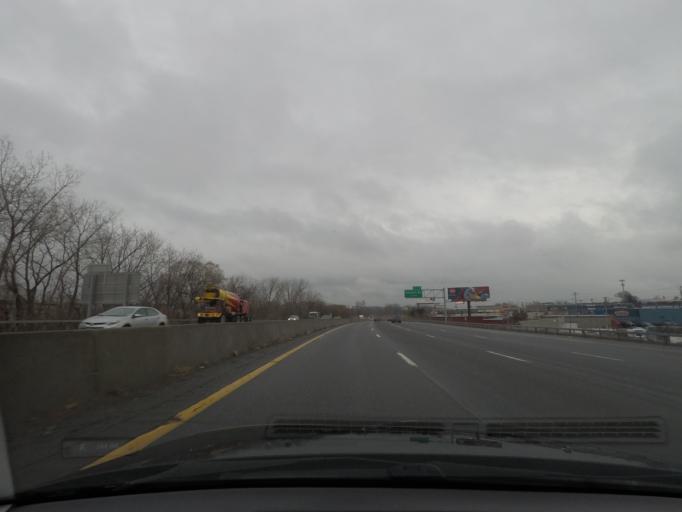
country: US
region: New York
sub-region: Albany County
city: Roessleville
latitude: 42.6870
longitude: -73.7972
